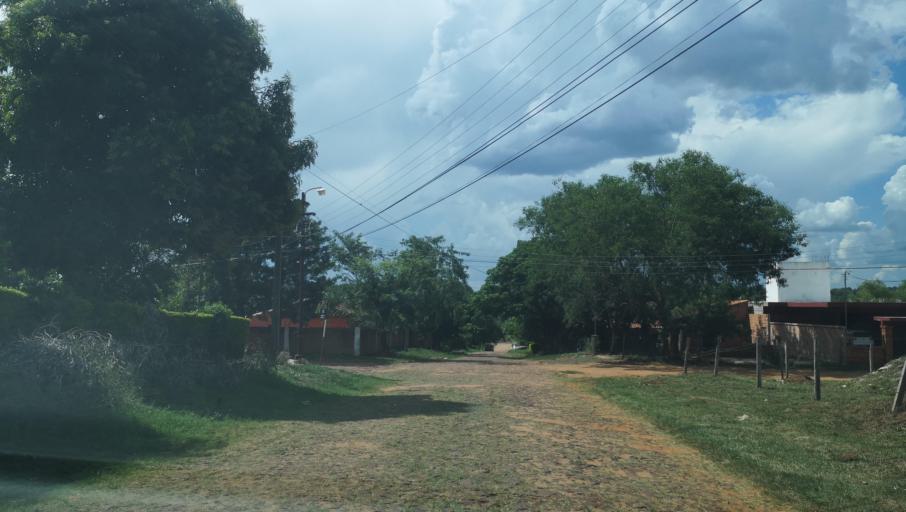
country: PY
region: Misiones
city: Santa Maria
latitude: -26.8877
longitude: -57.0142
